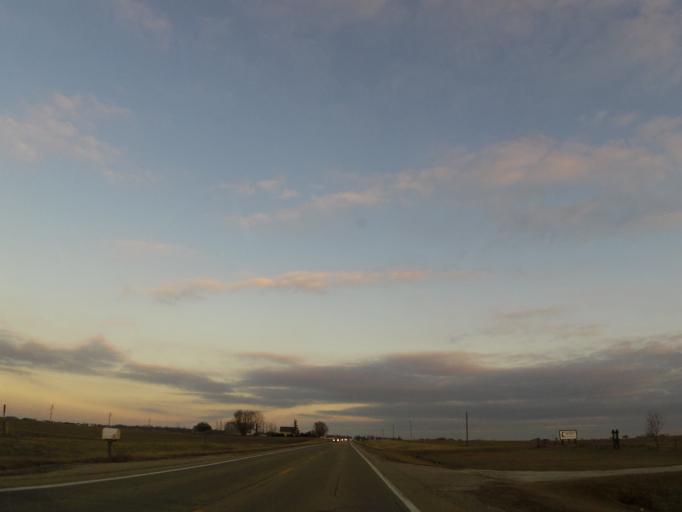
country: US
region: Illinois
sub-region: McLean County
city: Gridley
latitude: 40.7393
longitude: -88.9108
